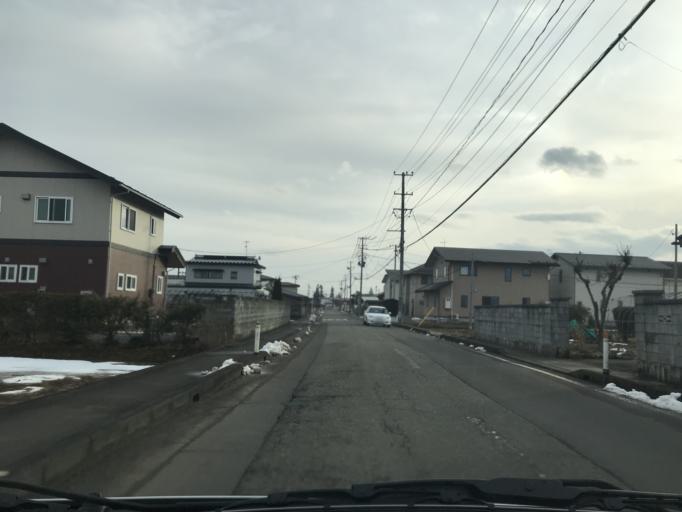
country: JP
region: Iwate
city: Mizusawa
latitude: 39.1679
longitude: 141.1293
